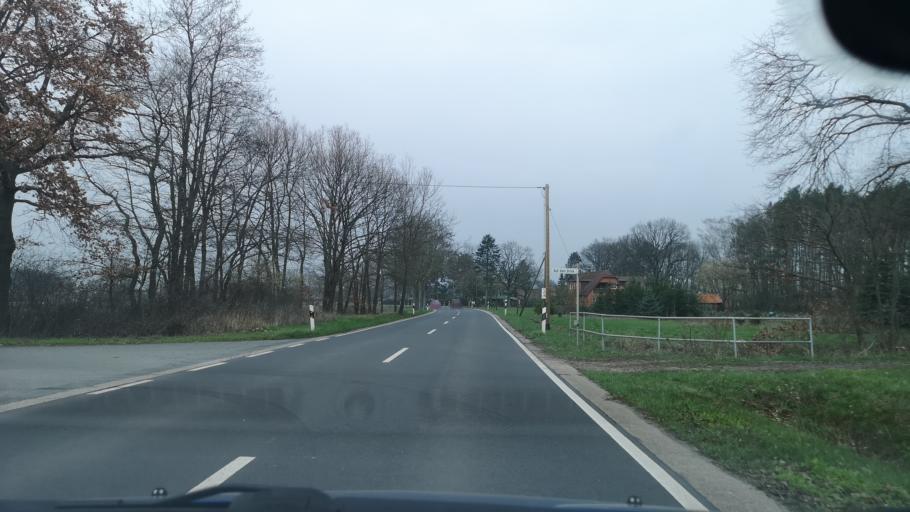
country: DE
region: Lower Saxony
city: Neustadt am Rubenberge
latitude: 52.4943
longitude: 9.5383
